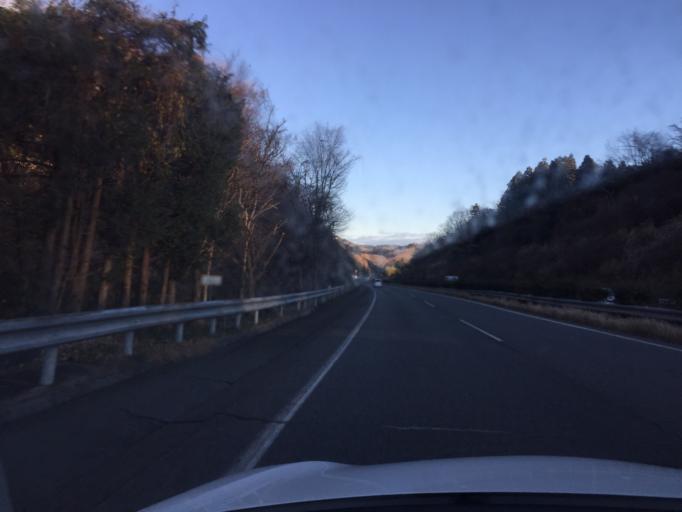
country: JP
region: Fukushima
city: Iwaki
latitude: 36.9746
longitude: 140.7941
